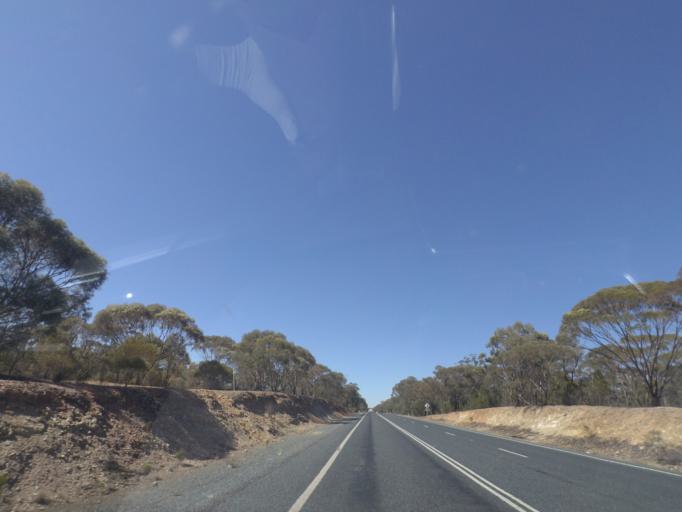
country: AU
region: New South Wales
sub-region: Bland
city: West Wyalong
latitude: -34.1281
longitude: 147.1246
